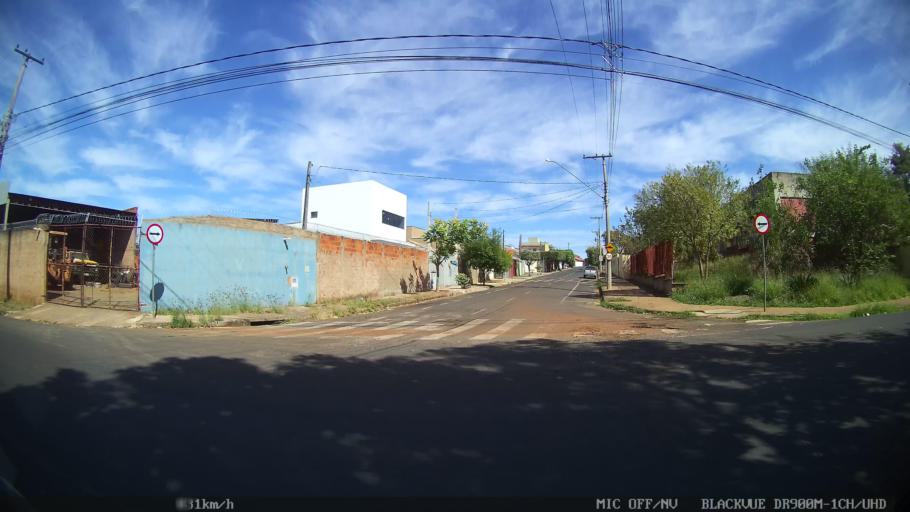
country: BR
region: Sao Paulo
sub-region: Sao Jose Do Rio Preto
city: Sao Jose do Rio Preto
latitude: -20.8440
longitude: -49.3606
